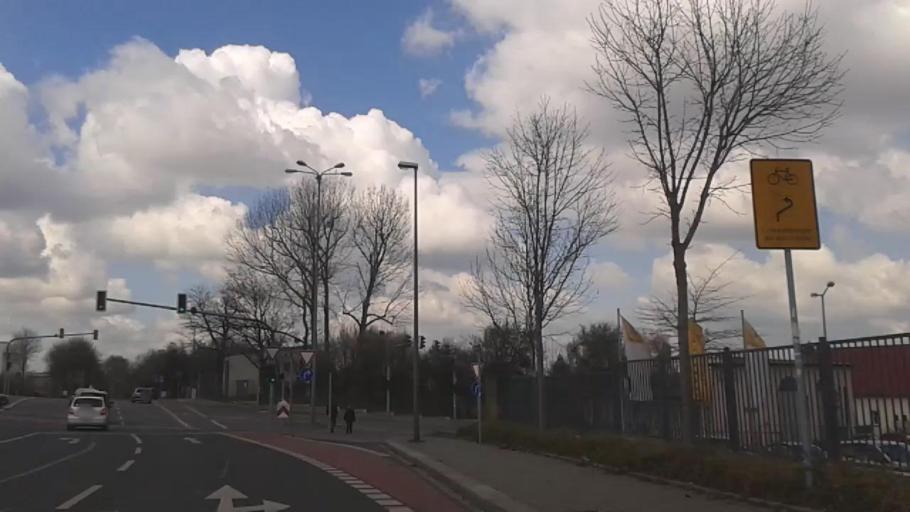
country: DE
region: Saxony
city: Dresden
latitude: 51.0247
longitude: 13.7322
